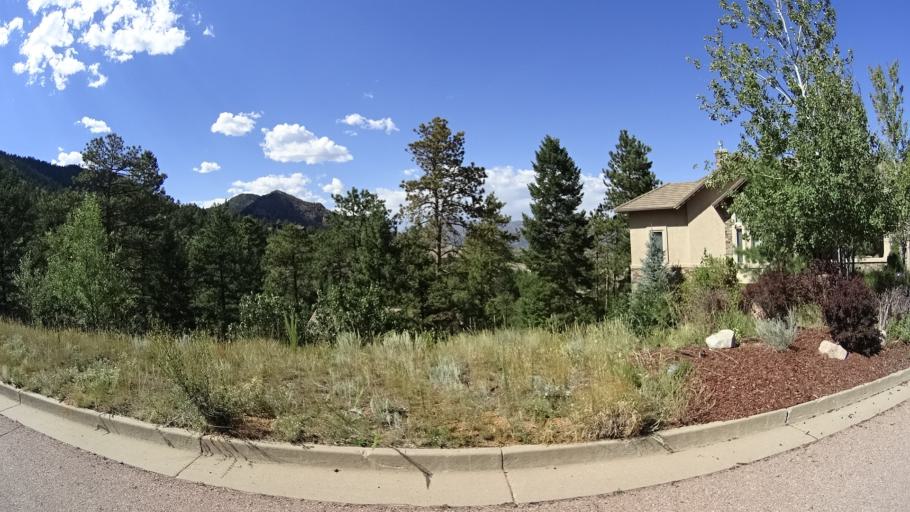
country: US
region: Colorado
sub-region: El Paso County
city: Manitou Springs
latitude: 38.8143
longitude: -104.8796
